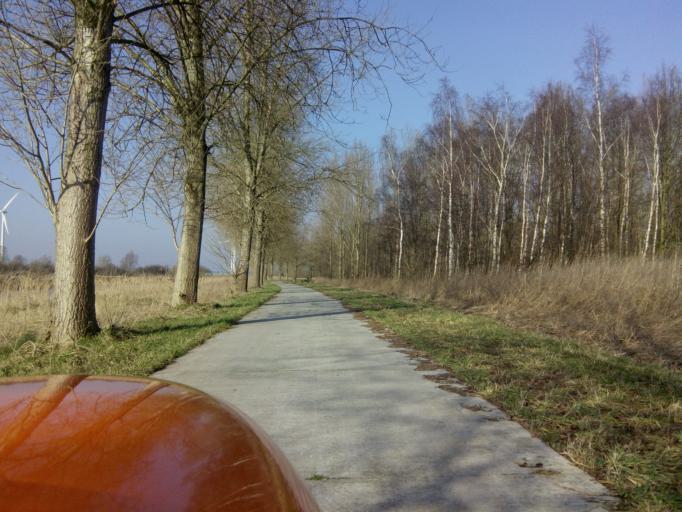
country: NL
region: Flevoland
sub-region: Gemeente Zeewolde
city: Zeewolde
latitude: 52.3323
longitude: 5.4447
